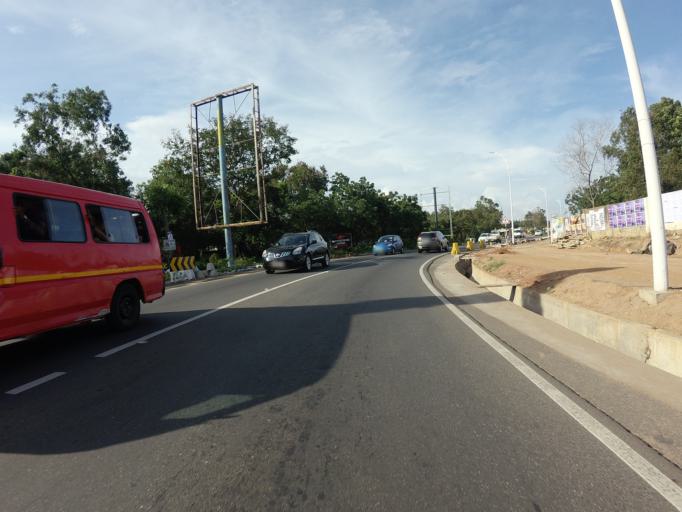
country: GH
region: Greater Accra
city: Medina Estates
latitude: 5.6272
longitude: -0.1587
